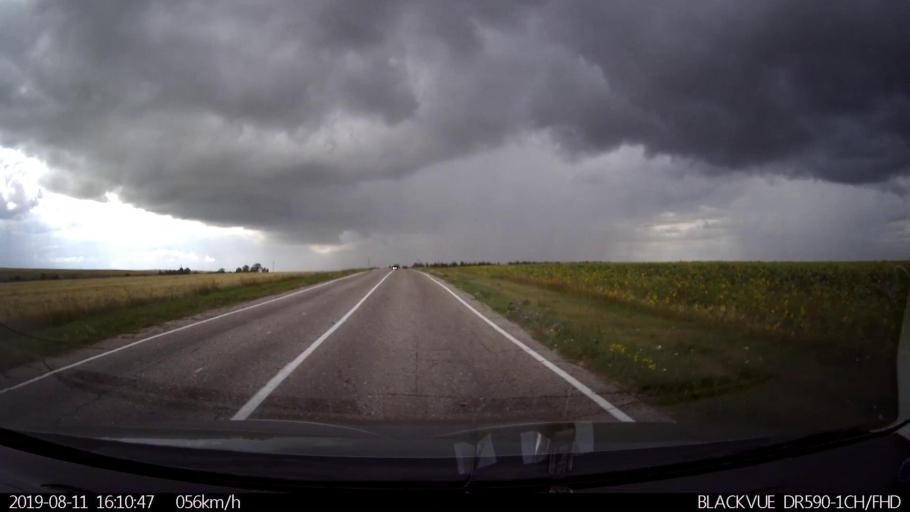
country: RU
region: Ulyanovsk
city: Ignatovka
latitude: 54.0000
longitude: 47.6512
